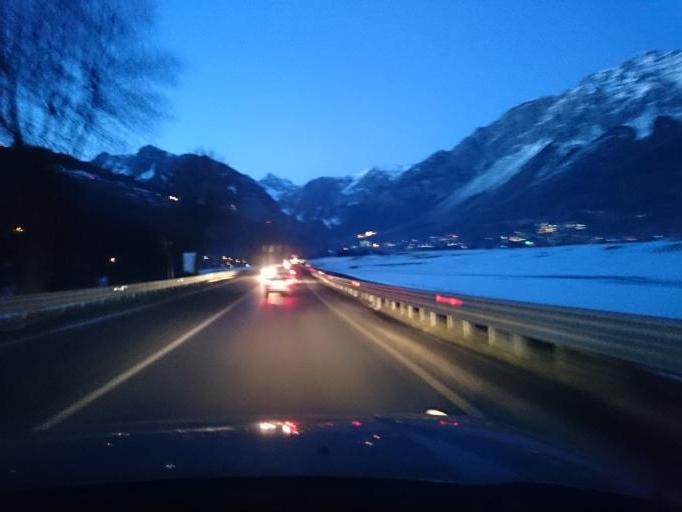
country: IT
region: Lombardy
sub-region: Provincia di Sondrio
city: Bormio
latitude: 46.4538
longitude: 10.3601
